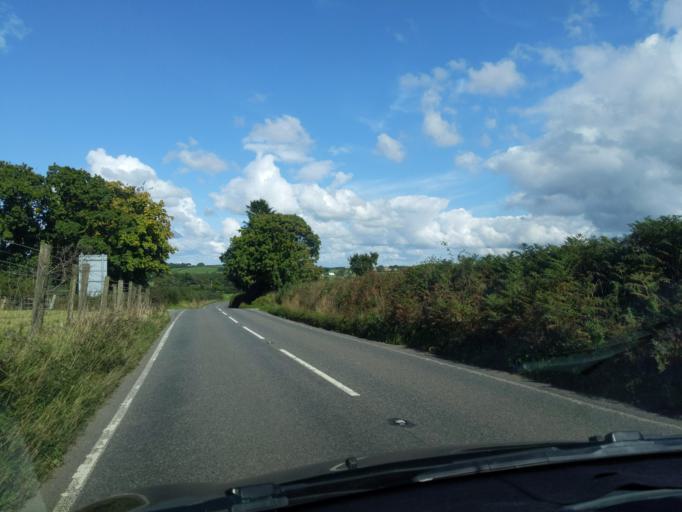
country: GB
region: England
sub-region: Cornwall
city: Launceston
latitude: 50.6510
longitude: -4.3481
